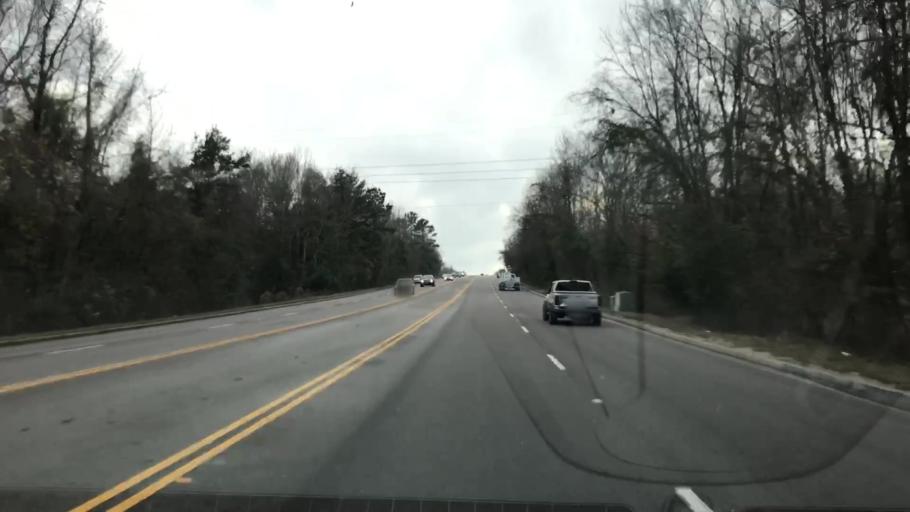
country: US
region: South Carolina
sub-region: Berkeley County
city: Moncks Corner
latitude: 33.2176
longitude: -79.9714
